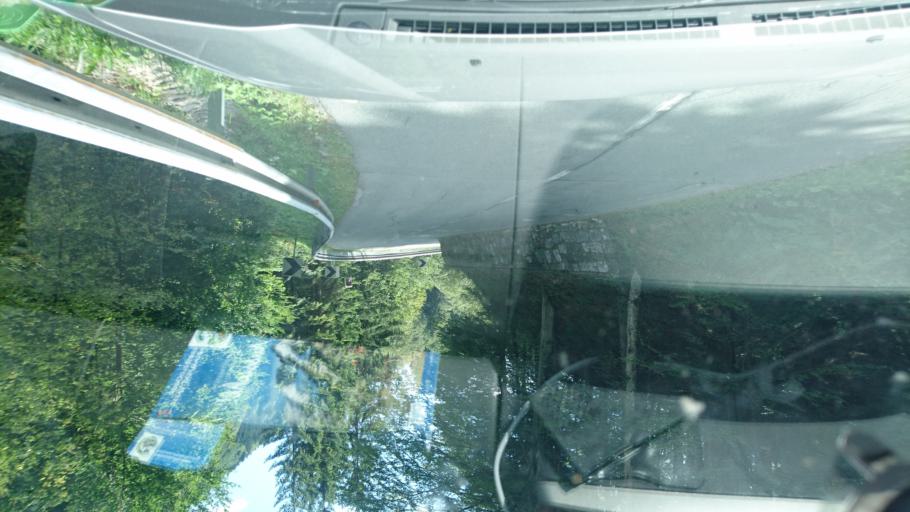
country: SI
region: Kranjska Gora
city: Kranjska Gora
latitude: 46.5038
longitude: 13.7548
